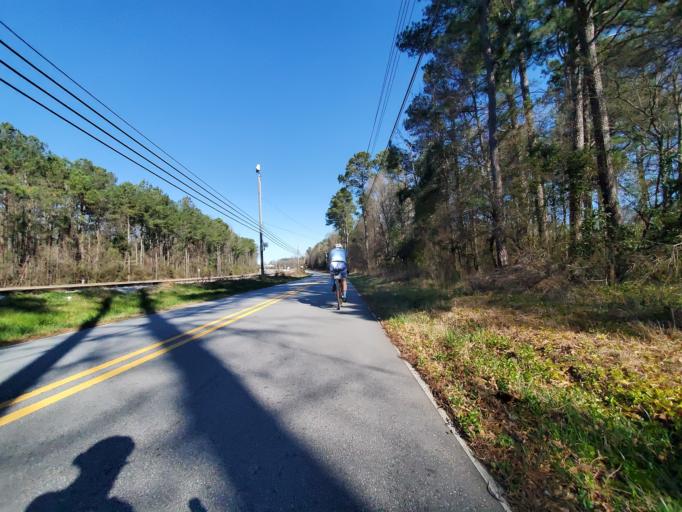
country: US
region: Georgia
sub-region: Clarke County
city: Country Club Estates
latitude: 33.9801
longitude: -83.4152
